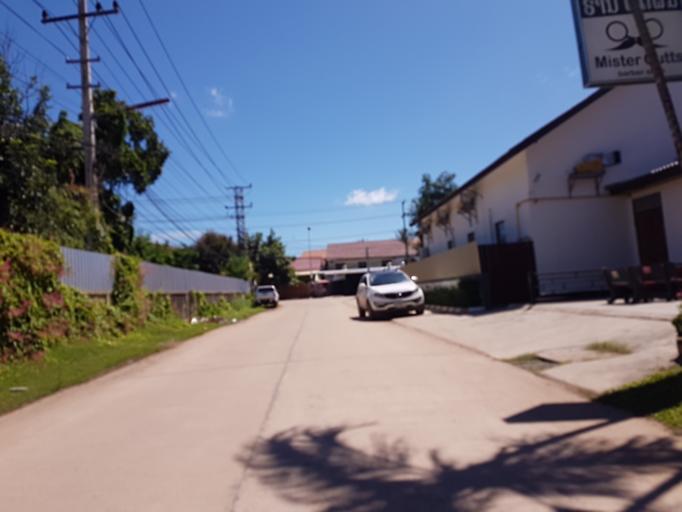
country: LA
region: Vientiane
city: Vientiane
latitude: 17.9432
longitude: 102.6293
